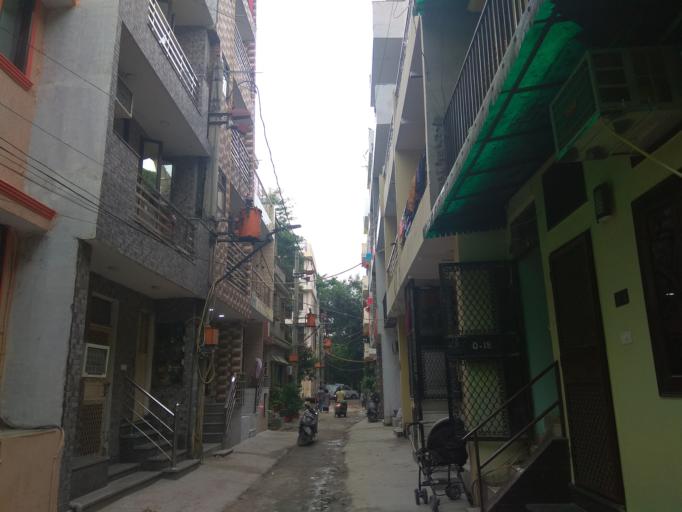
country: IN
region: NCT
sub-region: New Delhi
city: New Delhi
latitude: 28.5711
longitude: 77.2452
